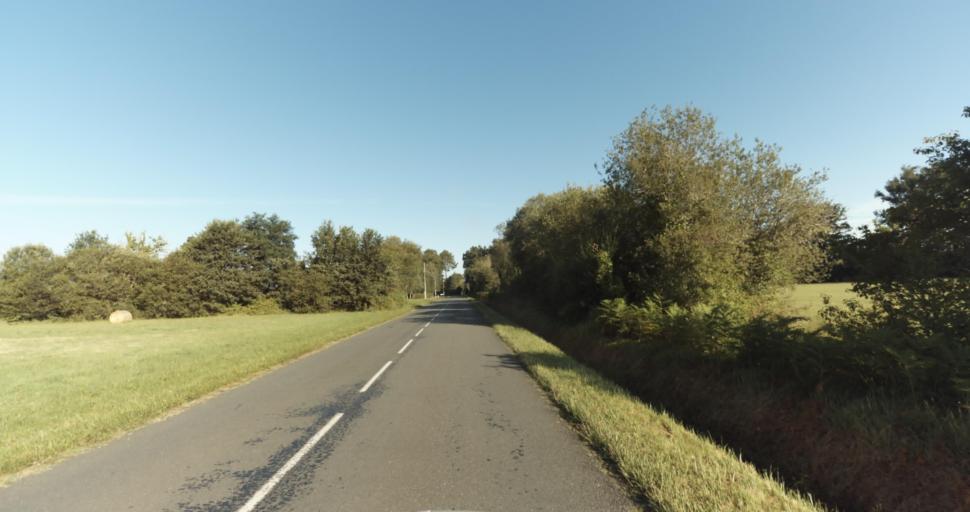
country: FR
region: Aquitaine
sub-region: Departement de la Gironde
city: Bazas
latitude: 44.4120
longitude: -0.2134
